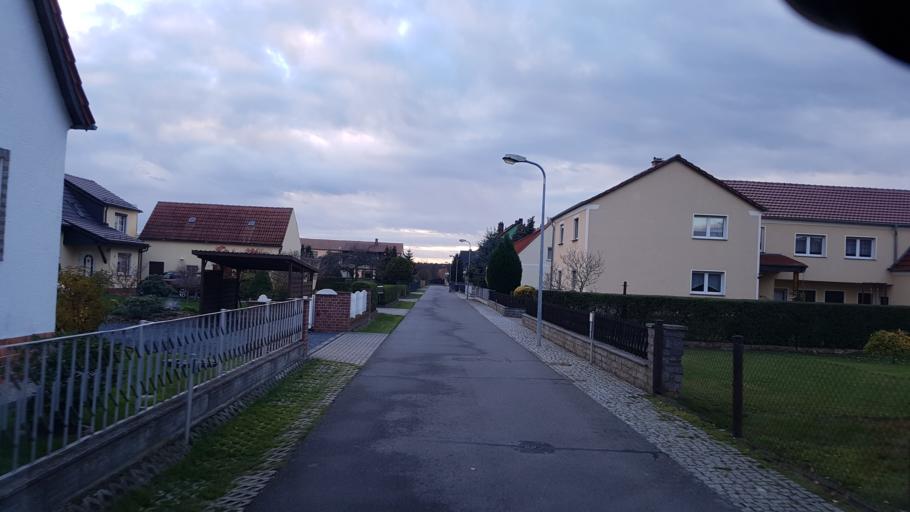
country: DE
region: Brandenburg
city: Lindenau
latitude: 51.4156
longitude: 13.7649
